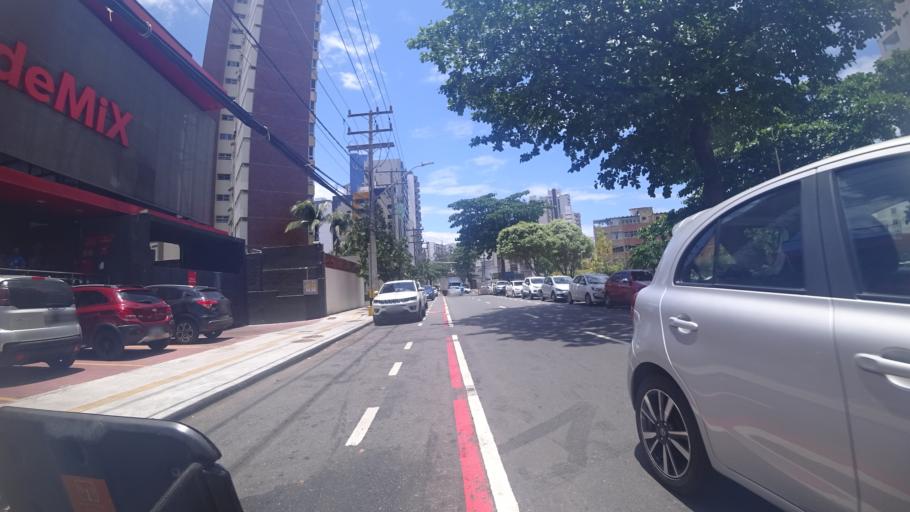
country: BR
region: Bahia
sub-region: Salvador
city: Salvador
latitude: -13.0042
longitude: -38.4597
